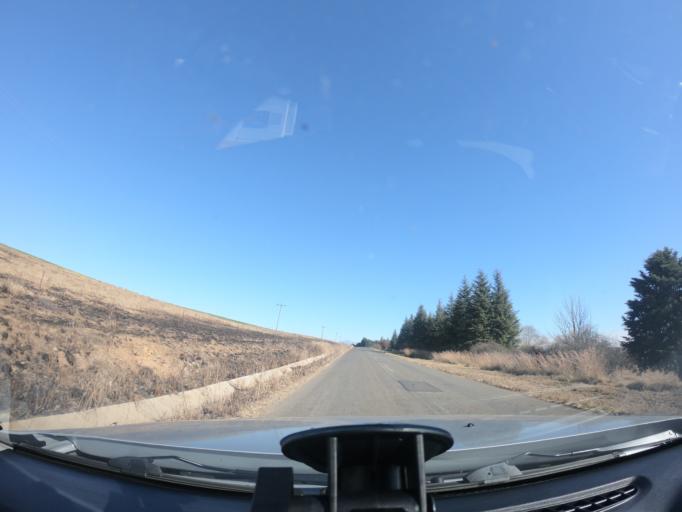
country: ZA
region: KwaZulu-Natal
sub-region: uMgungundlovu District Municipality
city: Mooirivier
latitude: -29.3257
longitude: 29.8596
